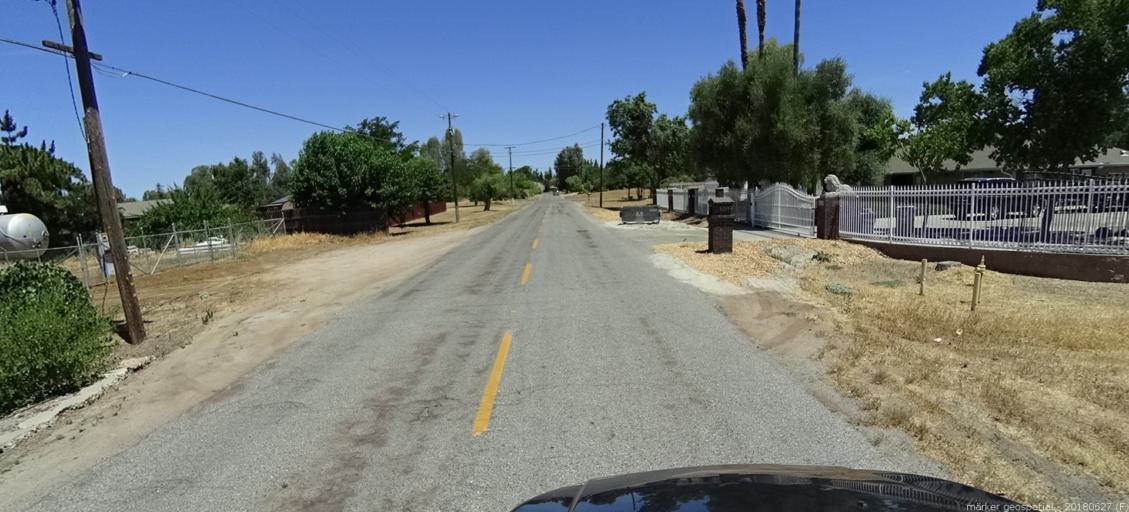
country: US
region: California
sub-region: Madera County
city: Bonadelle Ranchos-Madera Ranchos
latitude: 36.9256
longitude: -119.8692
